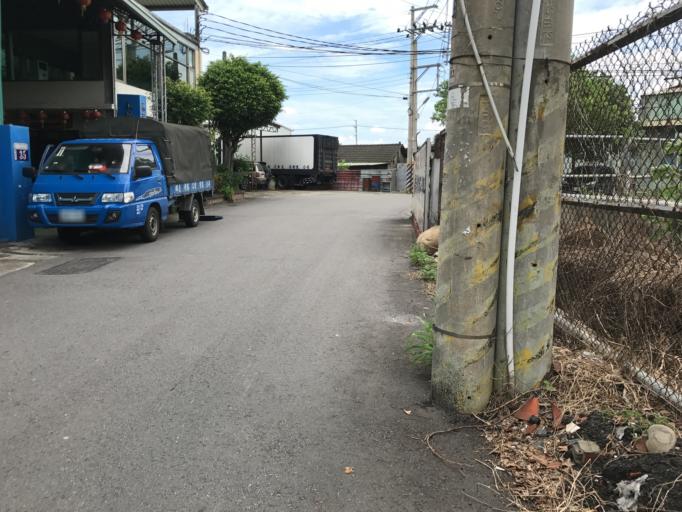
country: TW
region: Taiwan
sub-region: Taichung City
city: Taichung
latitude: 24.0793
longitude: 120.7132
